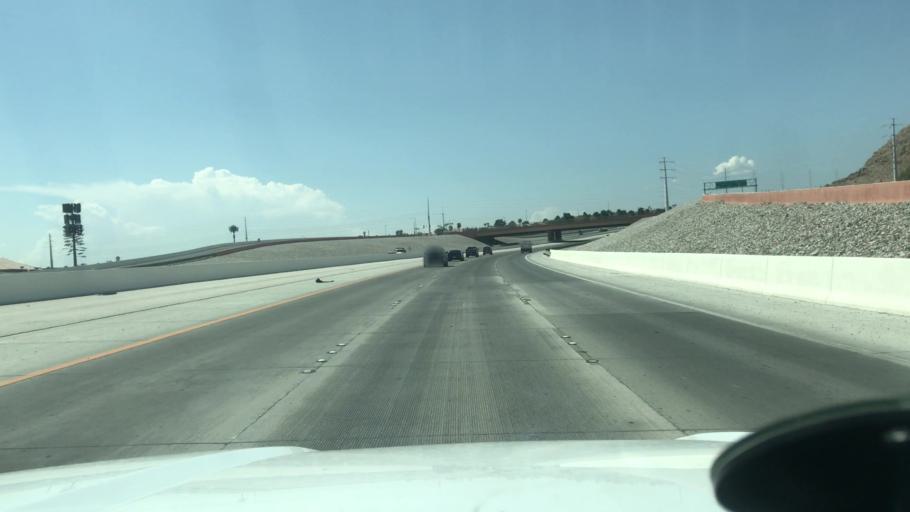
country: US
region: Nevada
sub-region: Clark County
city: Summerlin South
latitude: 36.2236
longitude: -115.3259
